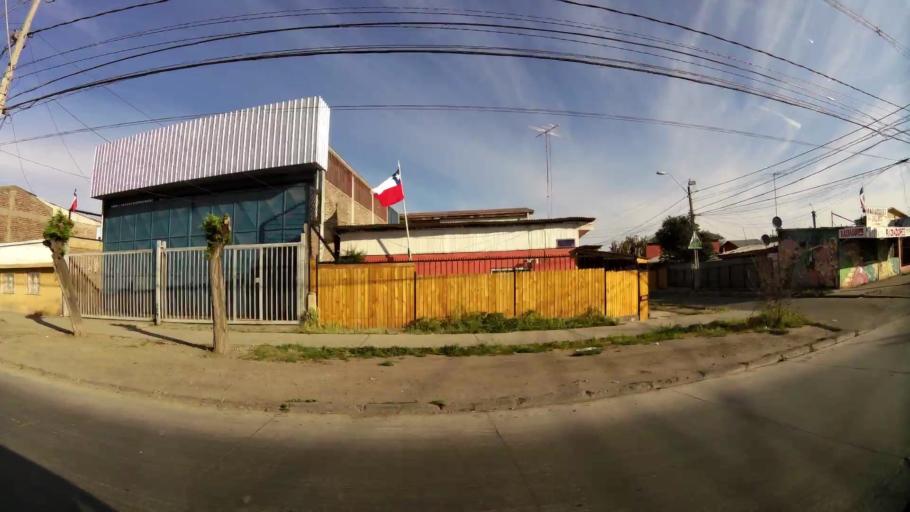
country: CL
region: Santiago Metropolitan
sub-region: Provincia de Cordillera
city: Puente Alto
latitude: -33.6190
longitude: -70.5758
